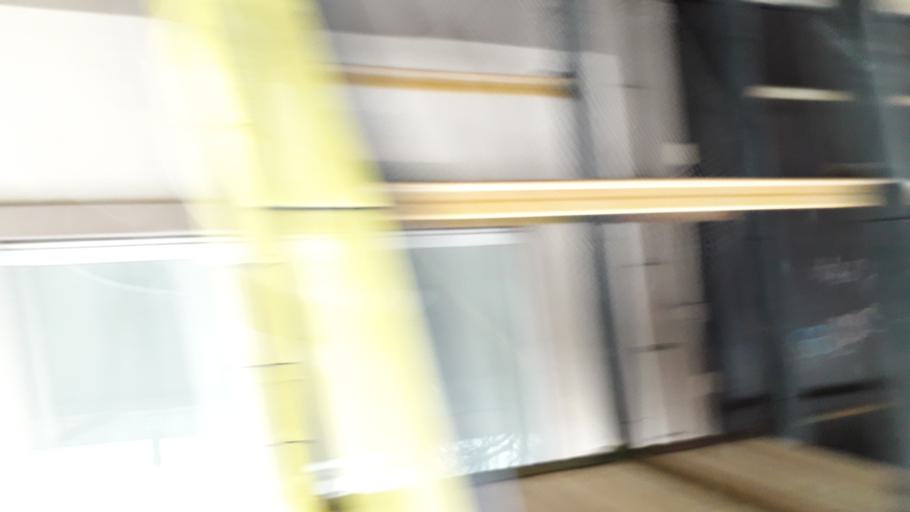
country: IE
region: Leinster
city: Rialto
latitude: 53.3432
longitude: -6.2929
